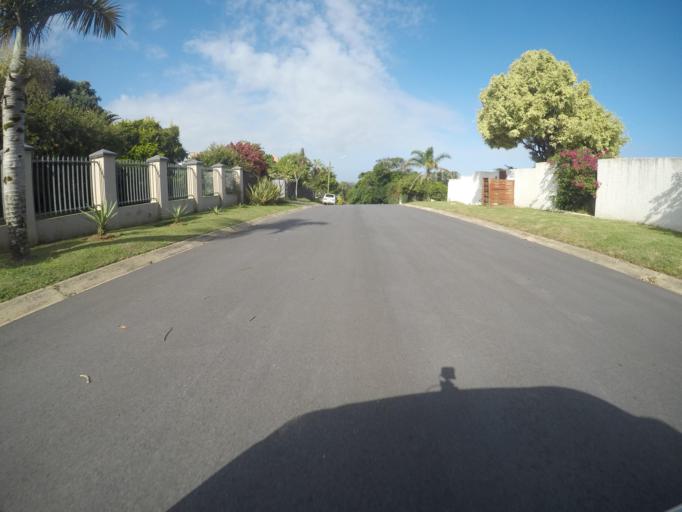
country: ZA
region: Eastern Cape
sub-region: Buffalo City Metropolitan Municipality
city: East London
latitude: -32.9730
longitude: 27.9542
